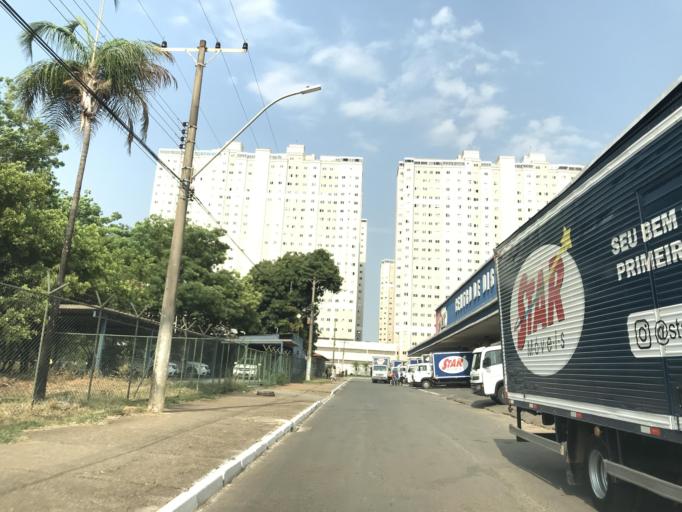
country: BR
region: Federal District
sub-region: Brasilia
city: Brasilia
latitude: -15.8116
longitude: -48.0778
